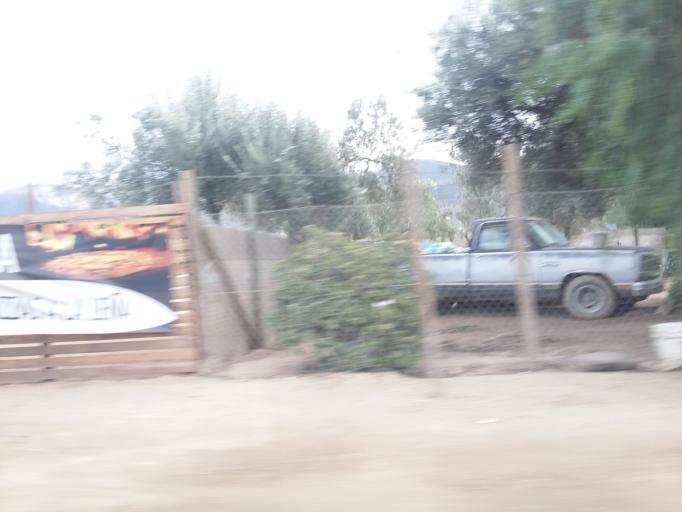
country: MX
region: Baja California
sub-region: Ensenada
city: Rancho Verde
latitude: 32.0922
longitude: -116.5786
